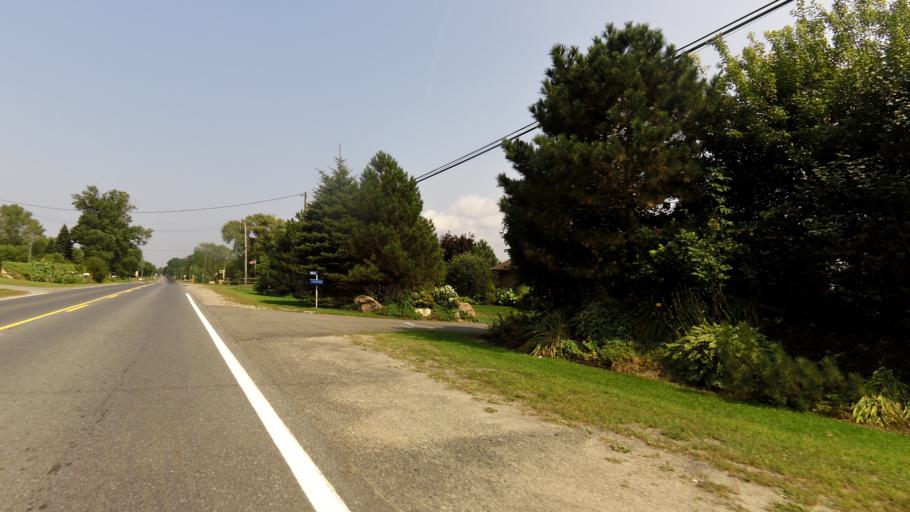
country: CA
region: Ontario
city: Prescott
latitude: 44.6927
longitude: -75.5447
